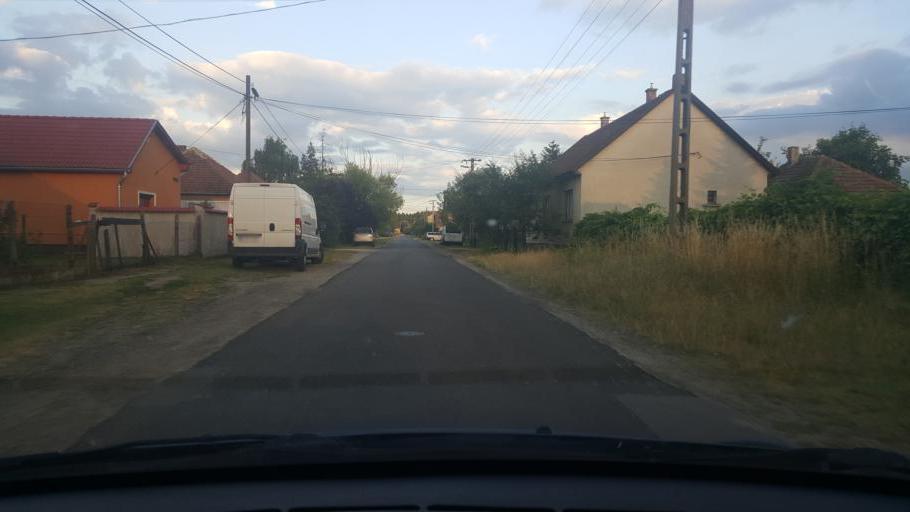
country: HU
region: Pest
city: Monor
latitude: 47.3356
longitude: 19.4428
